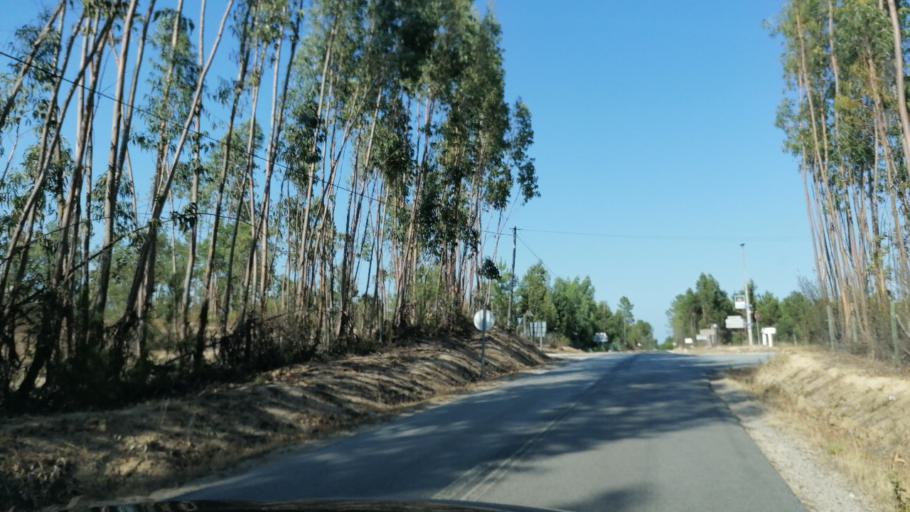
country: PT
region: Evora
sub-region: Vendas Novas
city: Vendas Novas
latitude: 38.7744
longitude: -8.5978
